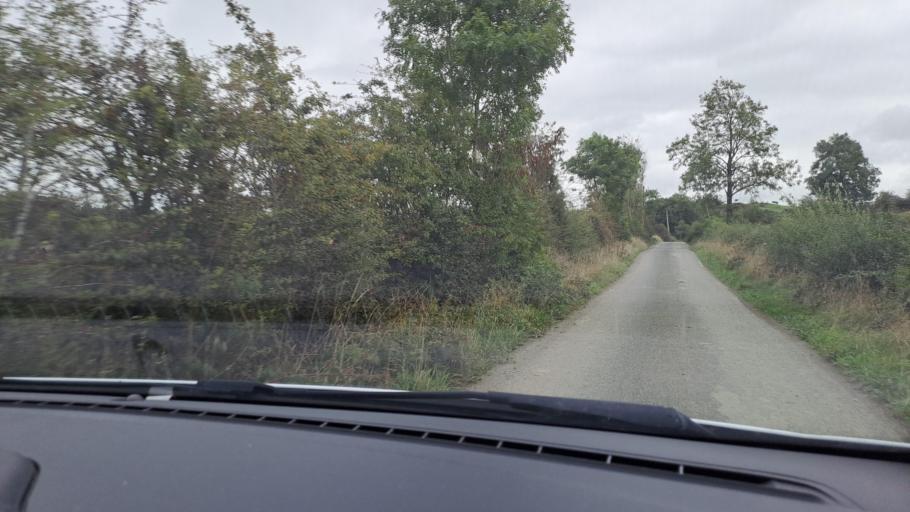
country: IE
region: Ulster
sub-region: County Monaghan
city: Castleblayney
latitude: 54.0420
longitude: -6.7965
